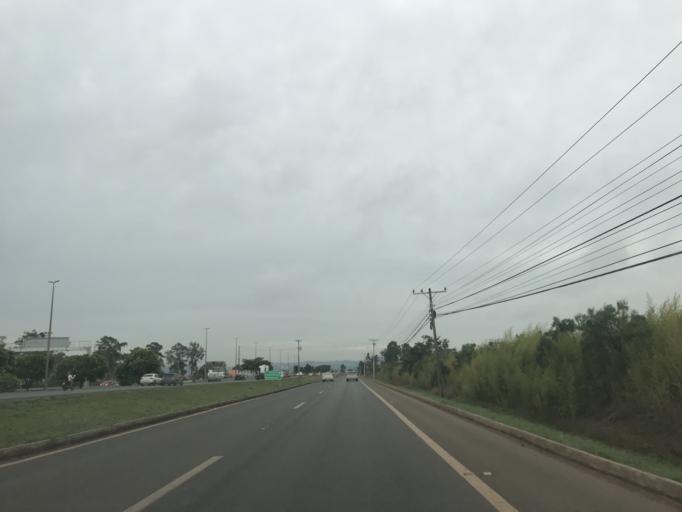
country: BR
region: Federal District
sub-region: Brasilia
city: Brasilia
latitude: -15.6852
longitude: -47.8473
